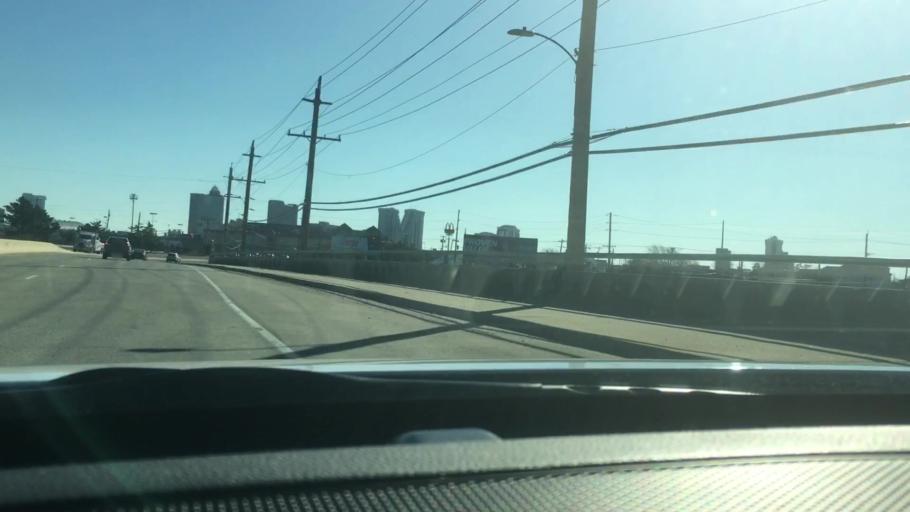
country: US
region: New Jersey
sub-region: Atlantic County
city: Ventnor City
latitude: 39.3613
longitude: -74.4646
